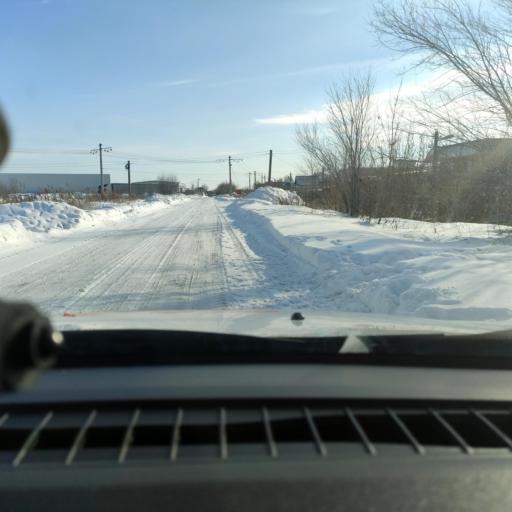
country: RU
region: Samara
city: Petra-Dubrava
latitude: 53.2632
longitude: 50.3511
